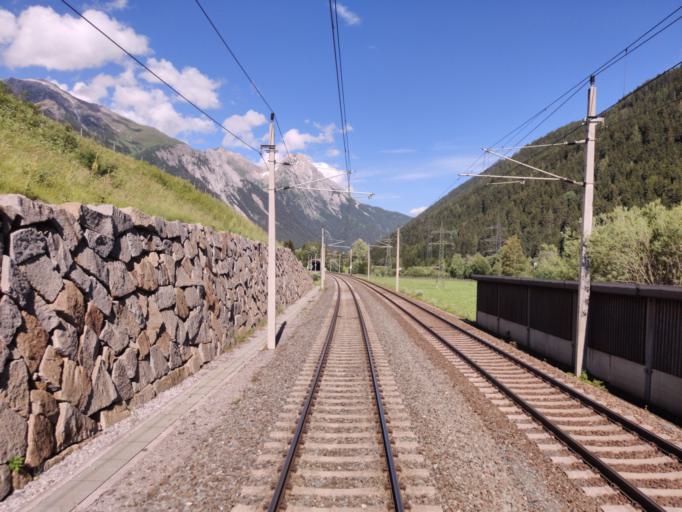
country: AT
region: Tyrol
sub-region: Politischer Bezirk Landeck
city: Flirsch
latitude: 47.1461
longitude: 10.3444
